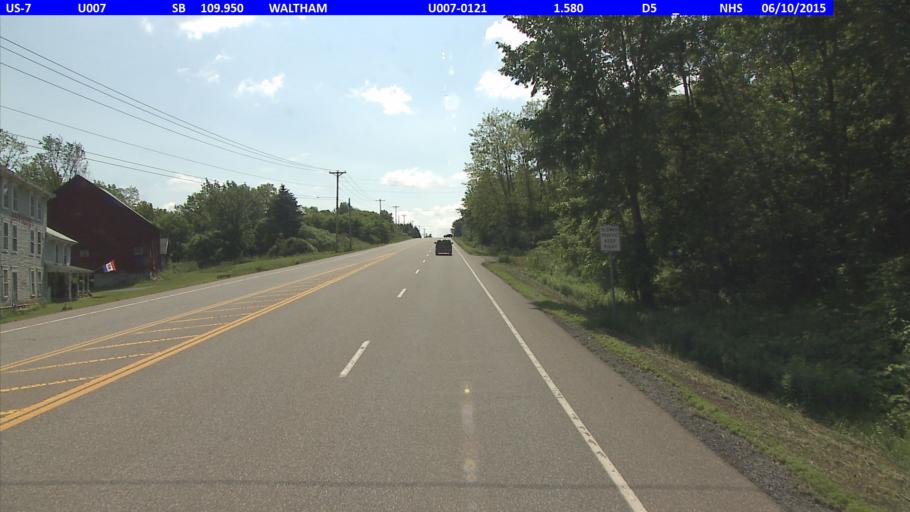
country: US
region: Vermont
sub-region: Addison County
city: Vergennes
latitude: 44.1630
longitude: -73.2350
